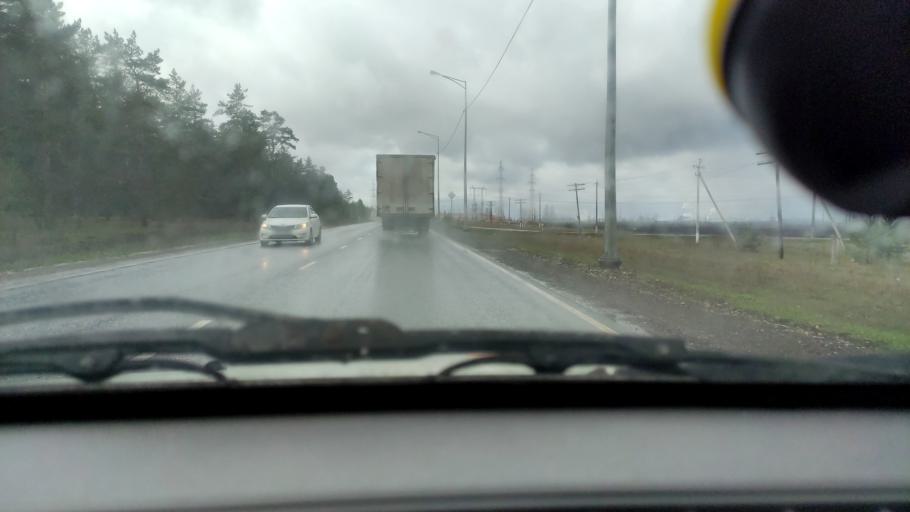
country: RU
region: Samara
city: Zhigulevsk
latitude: 53.5802
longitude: 49.5642
